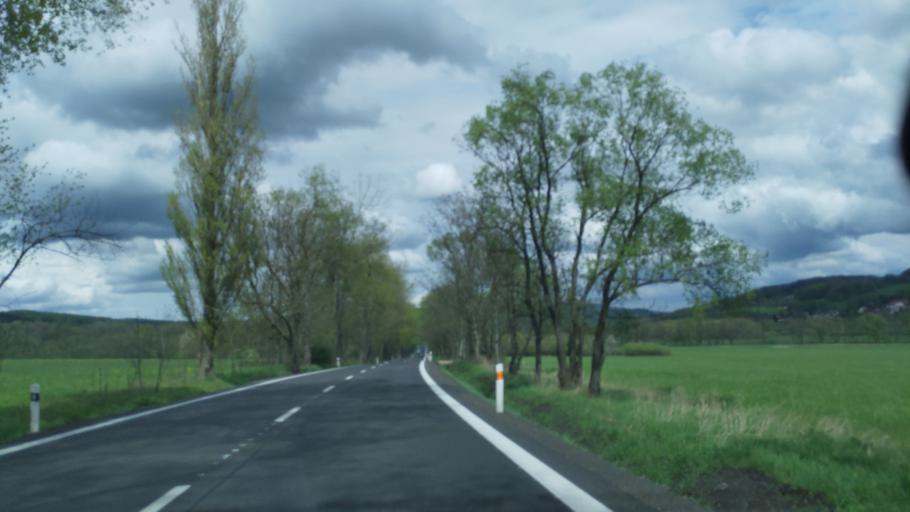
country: CZ
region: Ustecky
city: Libouchec
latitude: 50.7369
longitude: 14.0141
